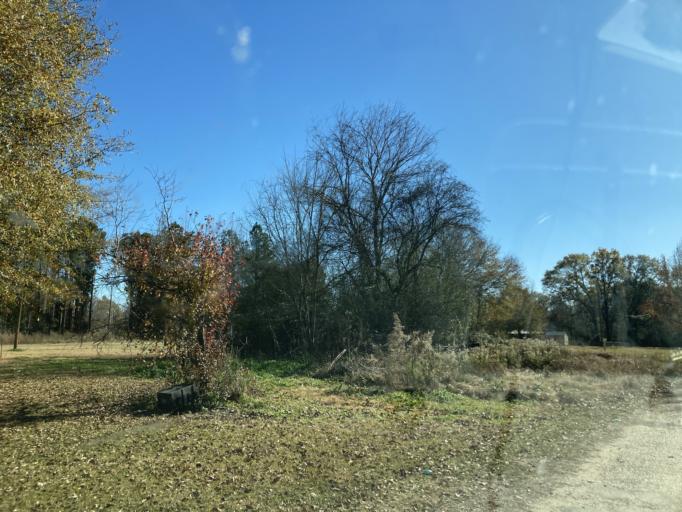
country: US
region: Mississippi
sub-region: Holmes County
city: Pickens
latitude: 32.8567
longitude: -90.0173
